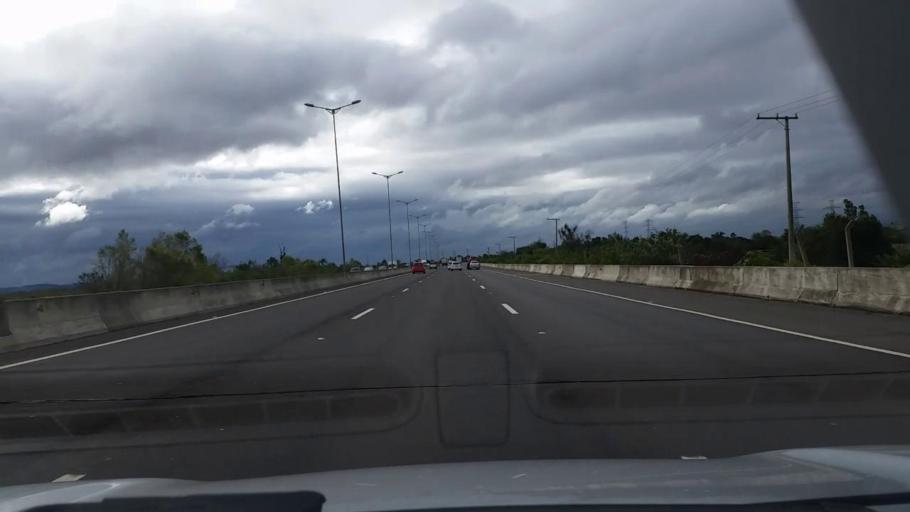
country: BR
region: Rio Grande do Sul
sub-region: Canoas
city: Canoas
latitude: -29.9473
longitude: -51.2039
